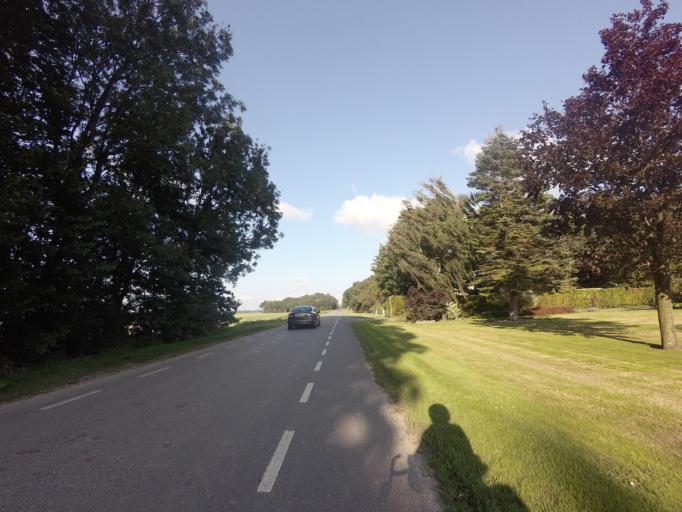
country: NL
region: Flevoland
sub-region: Gemeente Noordoostpolder
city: Ens
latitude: 52.6855
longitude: 5.8383
